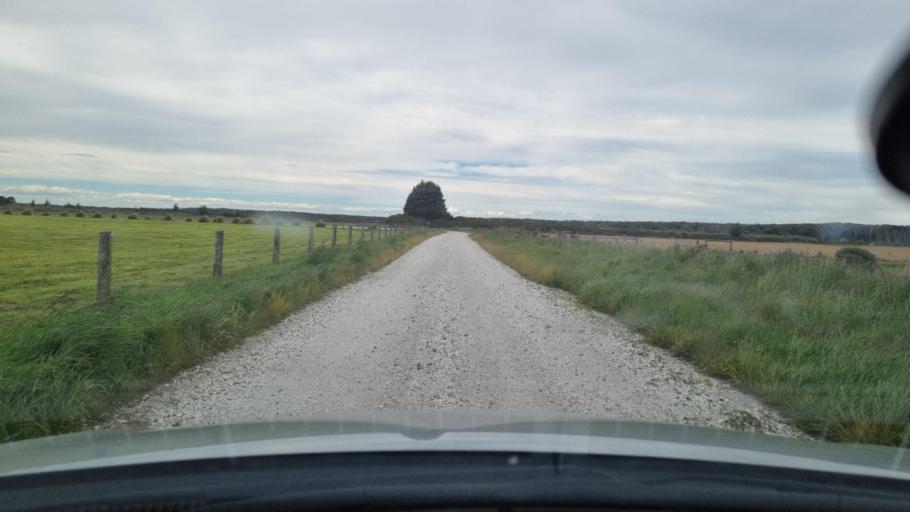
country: NZ
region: Southland
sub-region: Invercargill City
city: Invercargill
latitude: -46.5065
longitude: 168.4437
